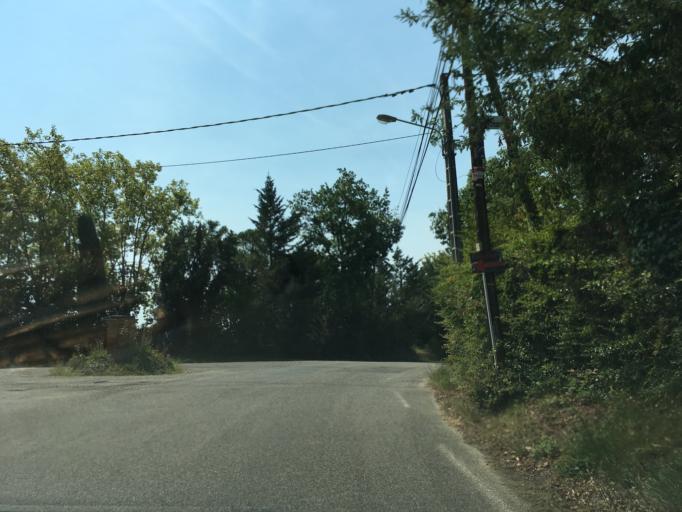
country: FR
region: Midi-Pyrenees
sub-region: Departement du Tarn-et-Garonne
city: Saint-Nauphary
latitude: 43.9899
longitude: 1.4214
